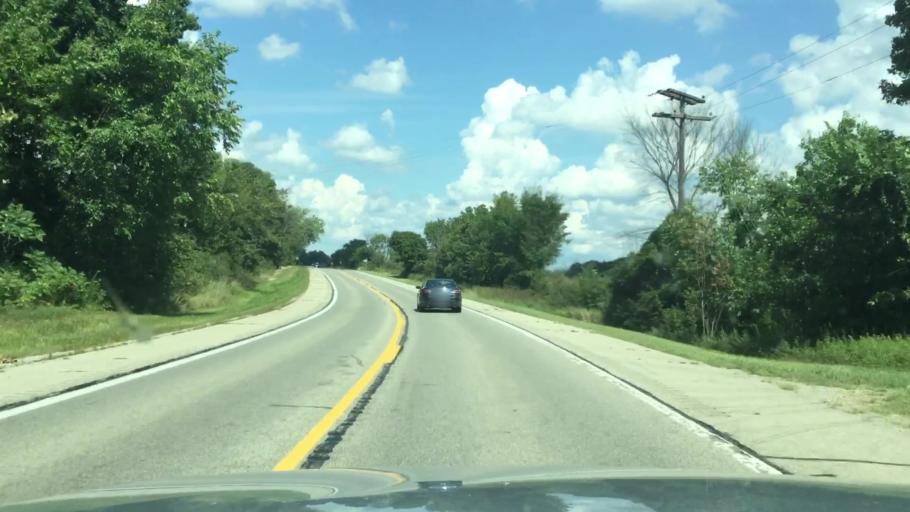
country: US
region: Michigan
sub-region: Lenawee County
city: Clinton
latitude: 42.0998
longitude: -83.9003
